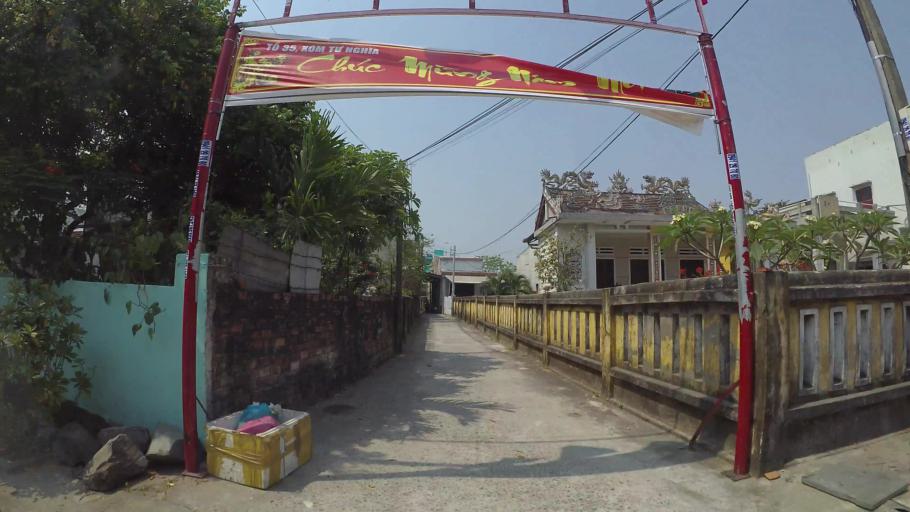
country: VN
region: Da Nang
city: Ngu Hanh Son
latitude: 16.0207
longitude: 108.2491
